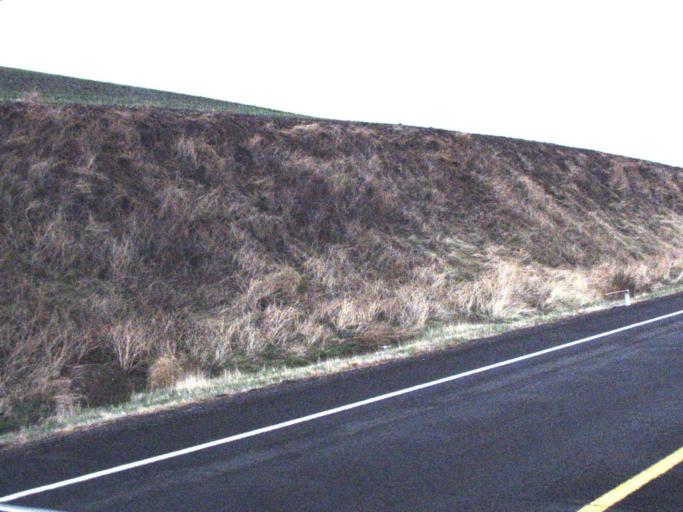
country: US
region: Washington
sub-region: Walla Walla County
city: Waitsburg
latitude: 46.2535
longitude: -118.1491
